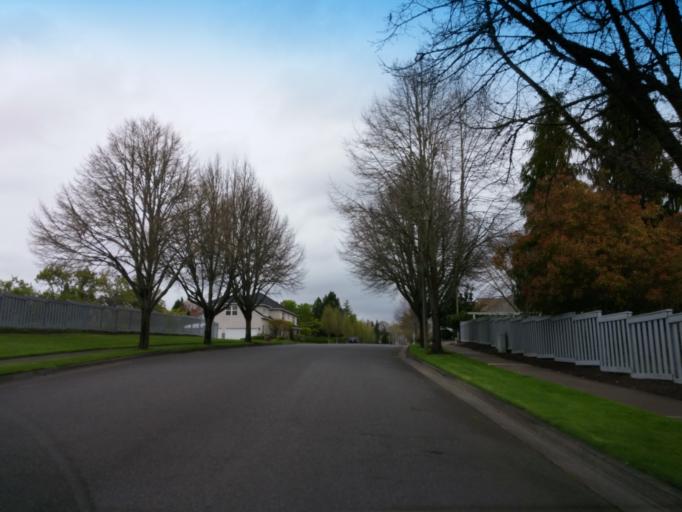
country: US
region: Oregon
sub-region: Washington County
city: Oak Hills
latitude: 45.5218
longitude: -122.8499
